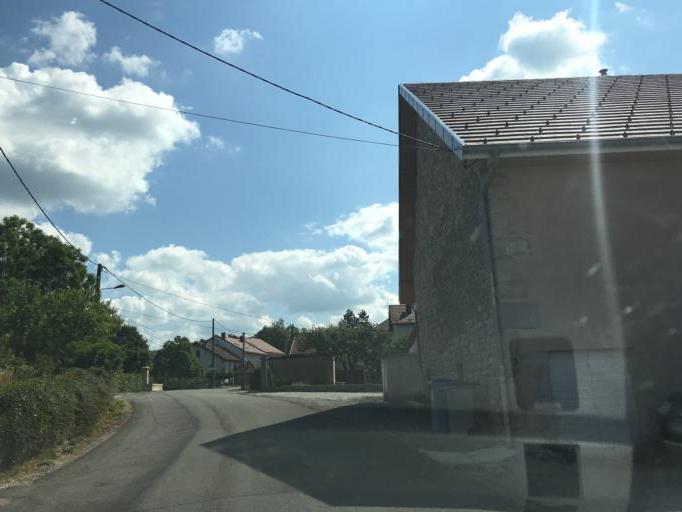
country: FR
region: Franche-Comte
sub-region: Departement du Jura
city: Moirans-en-Montagne
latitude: 46.4984
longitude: 5.7282
